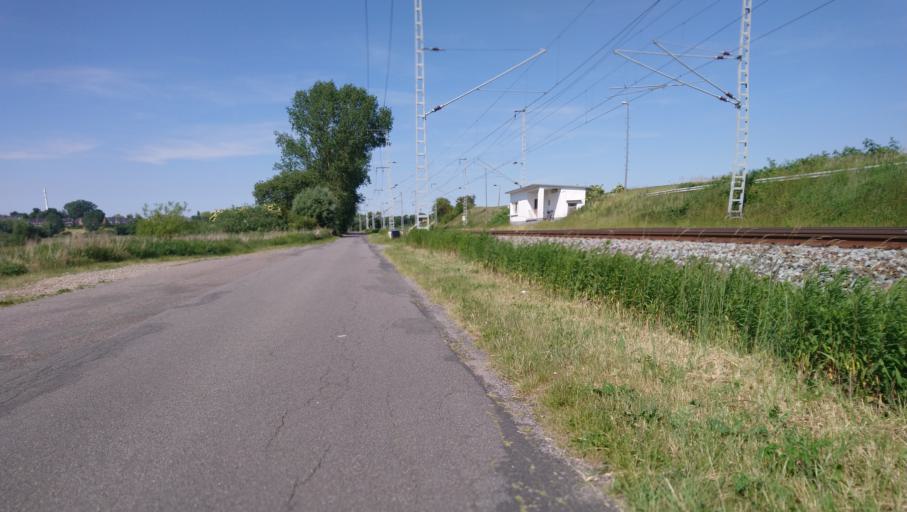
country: DE
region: Mecklenburg-Vorpommern
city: Dierkow-Neu
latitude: 54.0876
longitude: 12.1774
